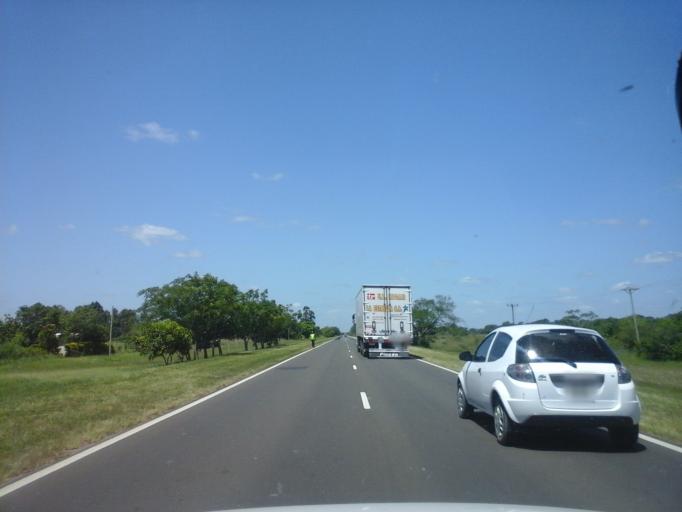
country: AR
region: Corrientes
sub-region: Departamento de Itati
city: Itati
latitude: -27.3397
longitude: -58.2116
